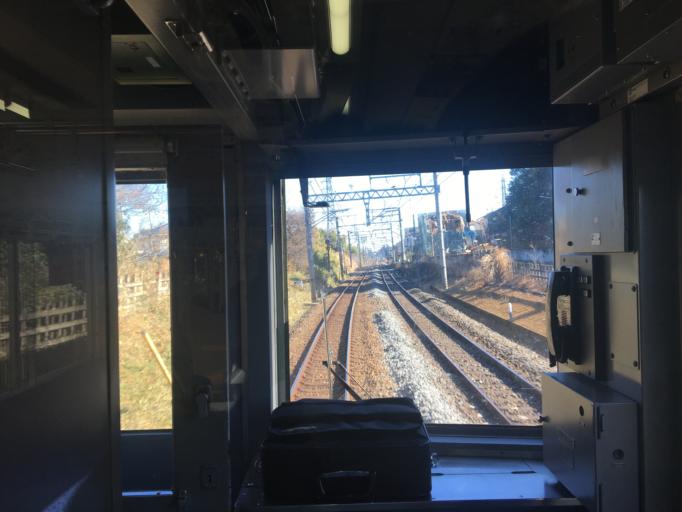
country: JP
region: Saitama
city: Iwatsuki
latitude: 35.9387
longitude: 139.6695
